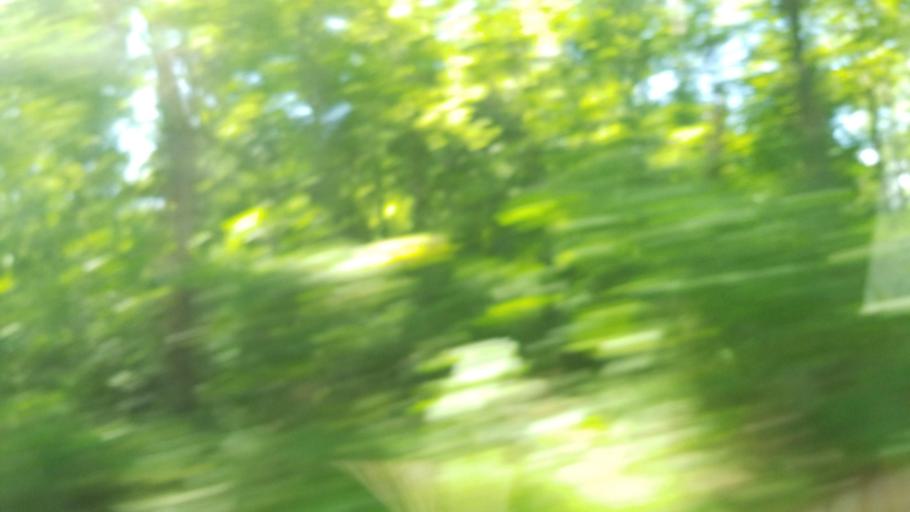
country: US
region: Illinois
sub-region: Williamson County
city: Johnston City
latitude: 37.7740
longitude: -88.8129
